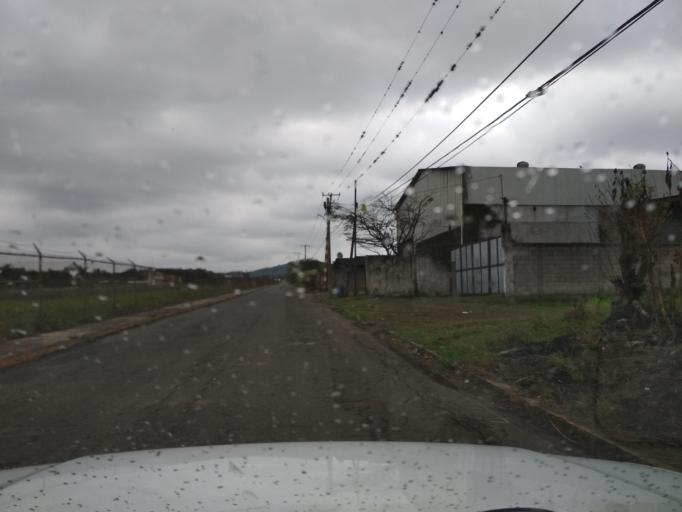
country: MX
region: Veracruz
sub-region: Cordoba
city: Veinte de Noviembre
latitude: 18.8713
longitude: -96.9541
